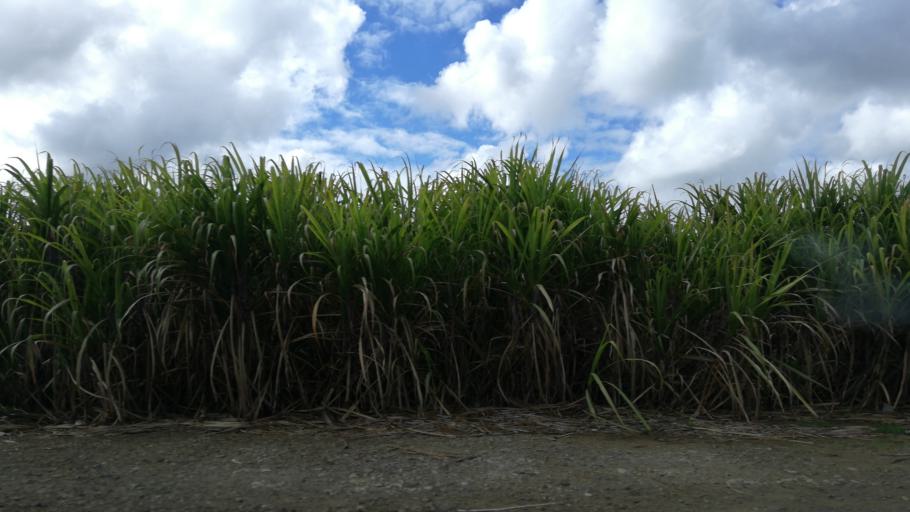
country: MU
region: Flacq
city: Lalmatie
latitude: -20.2117
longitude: 57.6768
